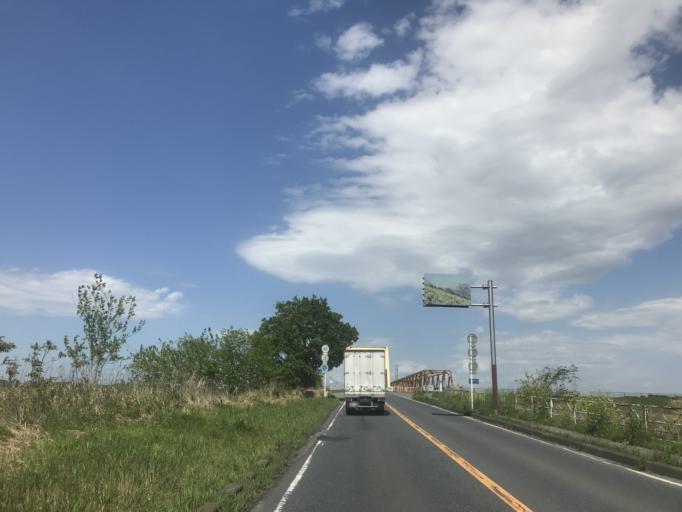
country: JP
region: Chiba
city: Noda
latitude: 35.9813
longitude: 139.8886
